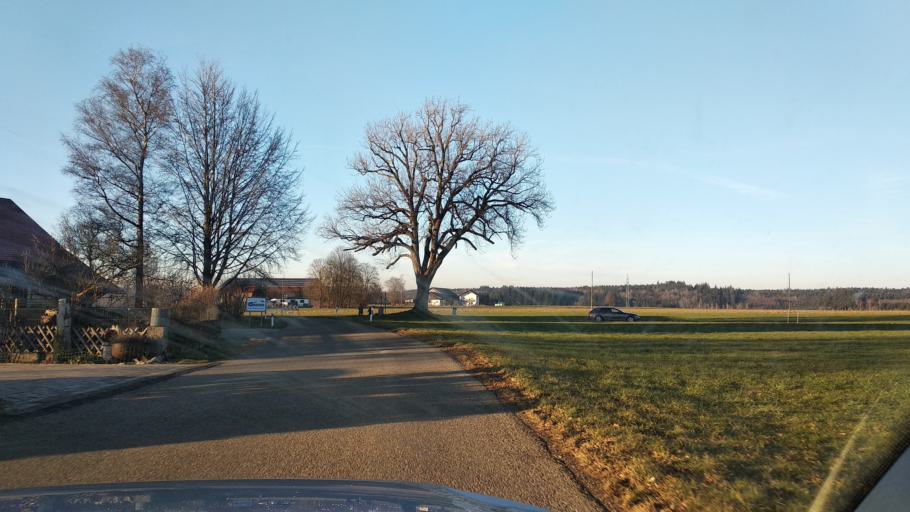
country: DE
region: Bavaria
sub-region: Swabia
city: Lautrach
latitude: 47.9196
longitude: 10.1279
